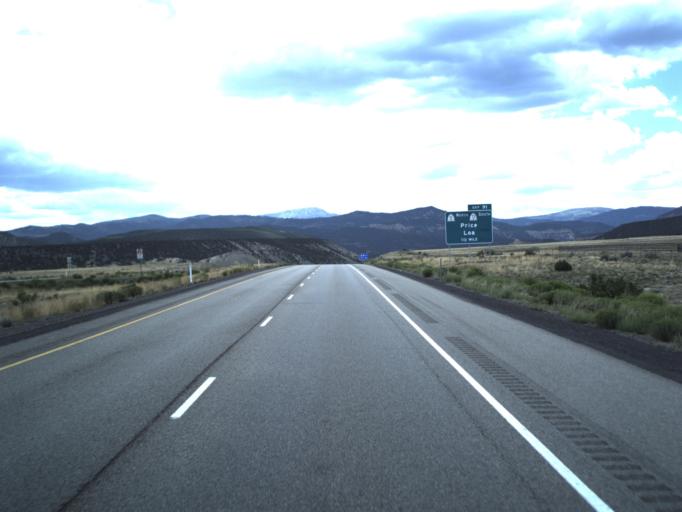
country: US
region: Utah
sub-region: Emery County
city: Ferron
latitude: 38.7715
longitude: -111.3340
